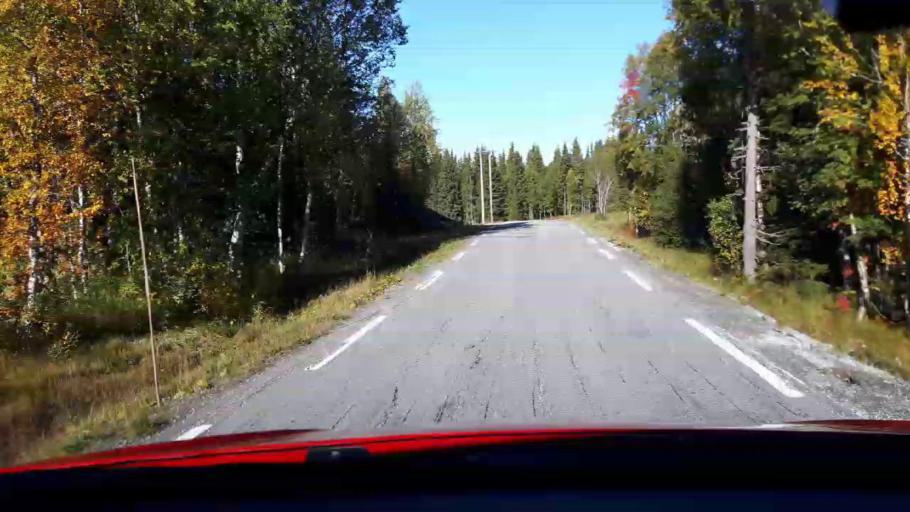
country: NO
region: Nord-Trondelag
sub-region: Lierne
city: Sandvika
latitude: 64.6235
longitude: 13.6918
